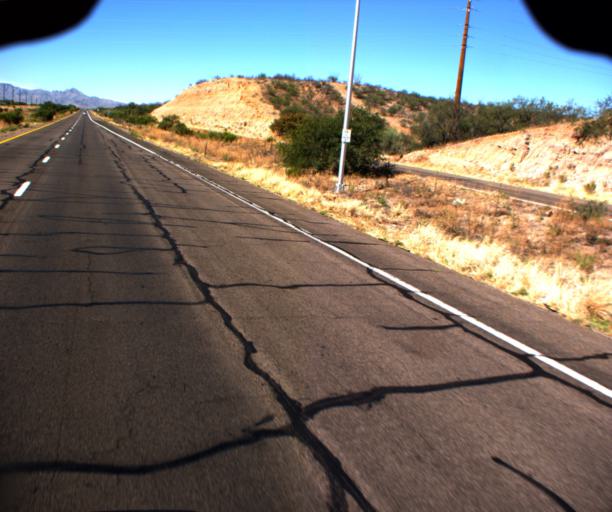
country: US
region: Arizona
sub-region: Pima County
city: Arivaca Junction
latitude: 31.7650
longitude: -111.0365
